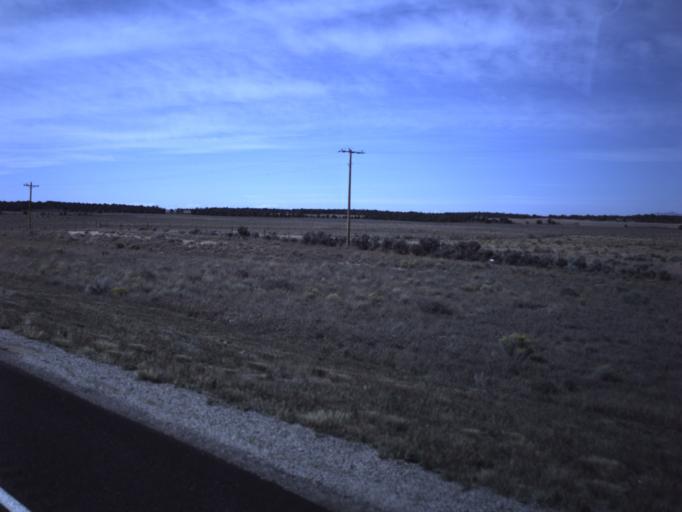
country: US
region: Colorado
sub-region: Dolores County
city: Dove Creek
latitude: 37.8327
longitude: -109.0982
